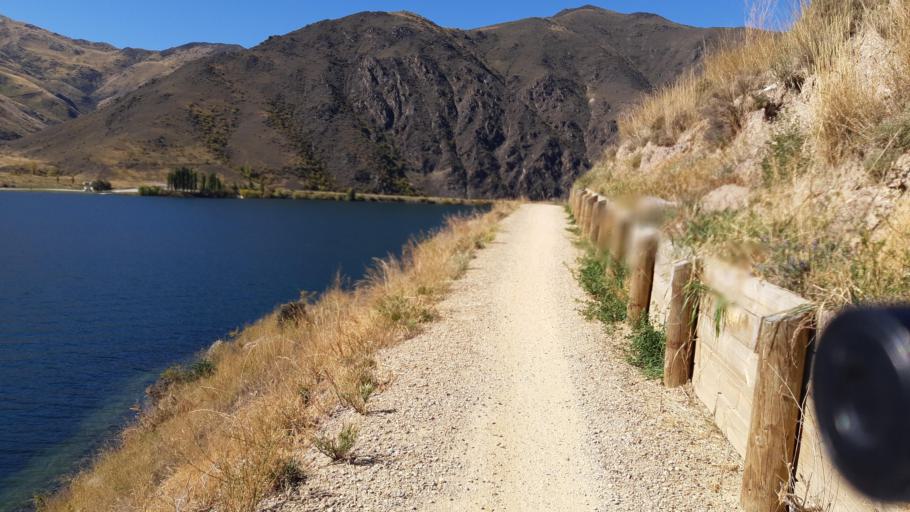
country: NZ
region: Otago
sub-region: Queenstown-Lakes District
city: Wanaka
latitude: -45.1308
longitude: 169.3093
